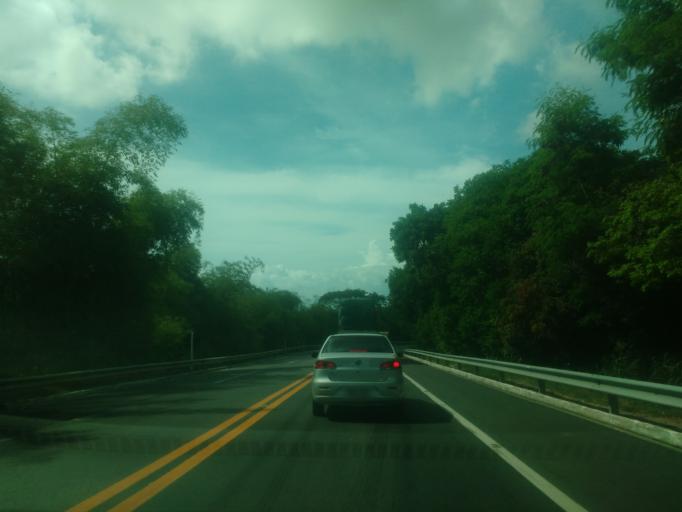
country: BR
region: Alagoas
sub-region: Marechal Deodoro
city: Marechal Deodoro
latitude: -9.6908
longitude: -35.8164
